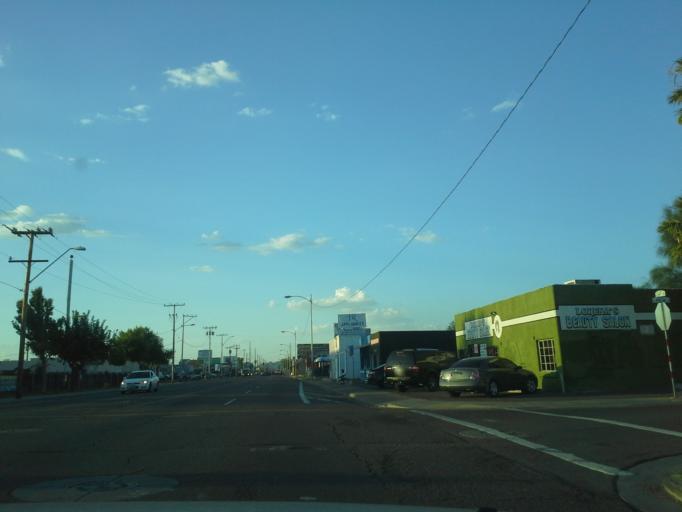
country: US
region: Arizona
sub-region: Maricopa County
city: Phoenix
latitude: 33.4692
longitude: -112.0476
